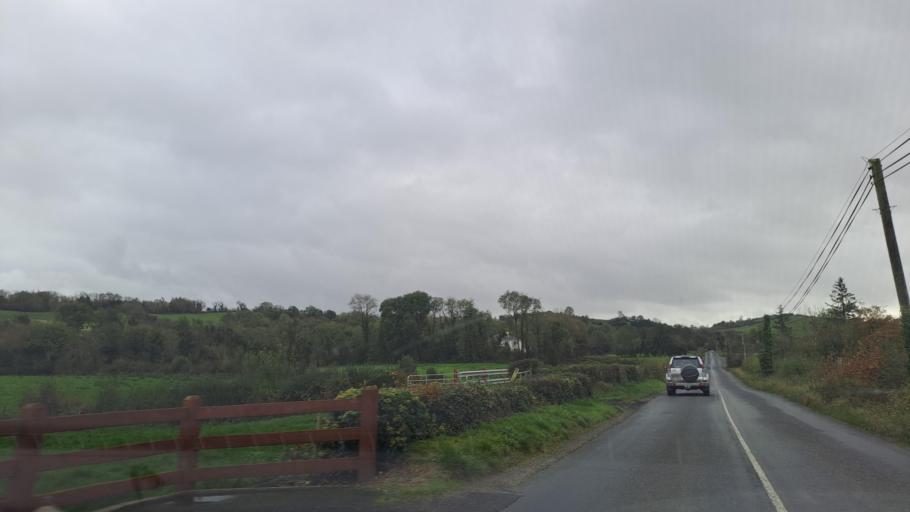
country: IE
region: Ulster
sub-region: An Cabhan
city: Bailieborough
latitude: 53.9684
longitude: -7.0428
